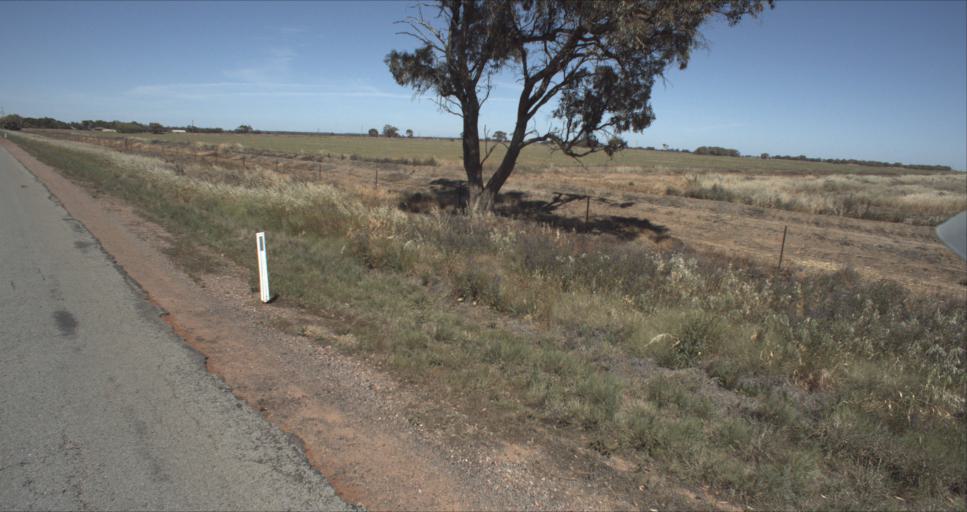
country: AU
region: New South Wales
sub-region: Leeton
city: Leeton
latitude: -34.5630
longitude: 146.3123
